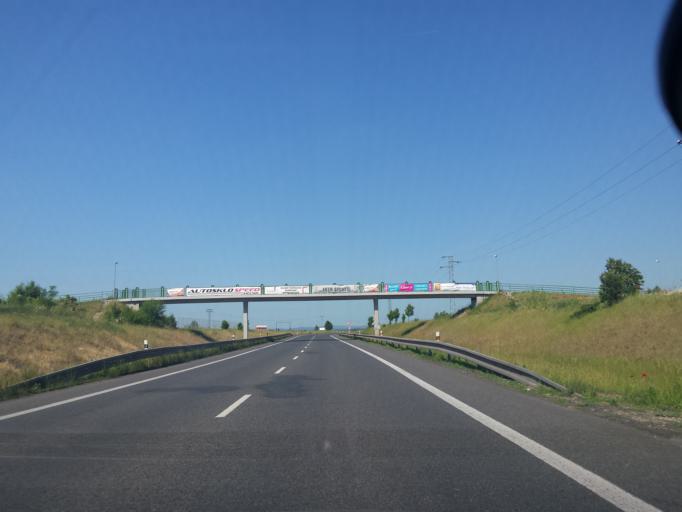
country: CZ
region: Central Bohemia
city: Luzec nad Vltavou
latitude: 50.3344
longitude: 14.3680
